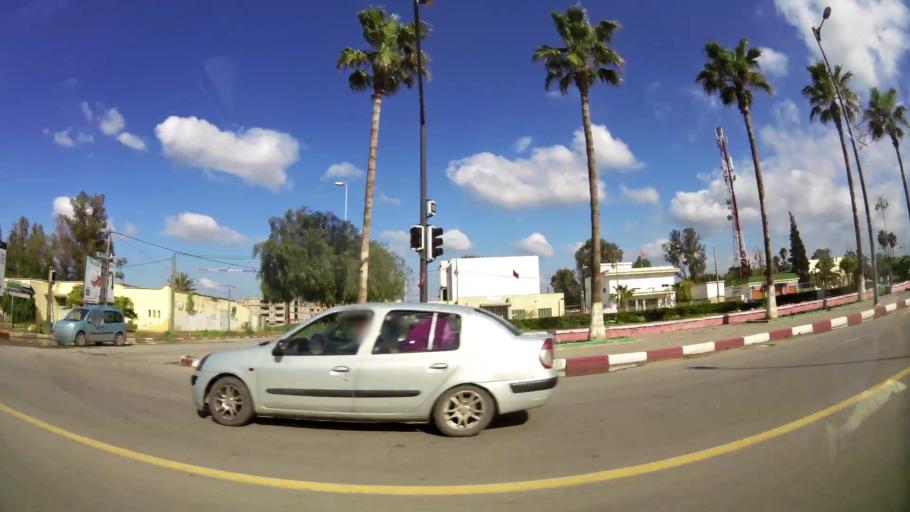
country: MA
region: Grand Casablanca
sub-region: Mediouna
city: Mediouna
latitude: 33.3756
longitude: -7.5413
